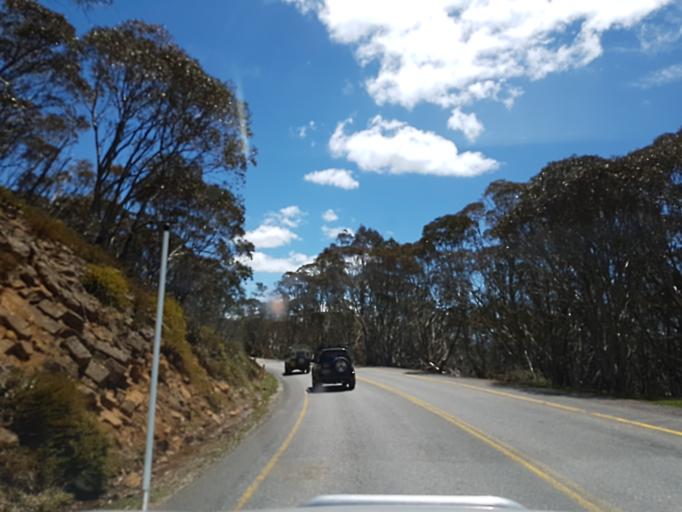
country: AU
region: Victoria
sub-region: Alpine
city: Mount Beauty
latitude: -37.0165
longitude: 147.1933
